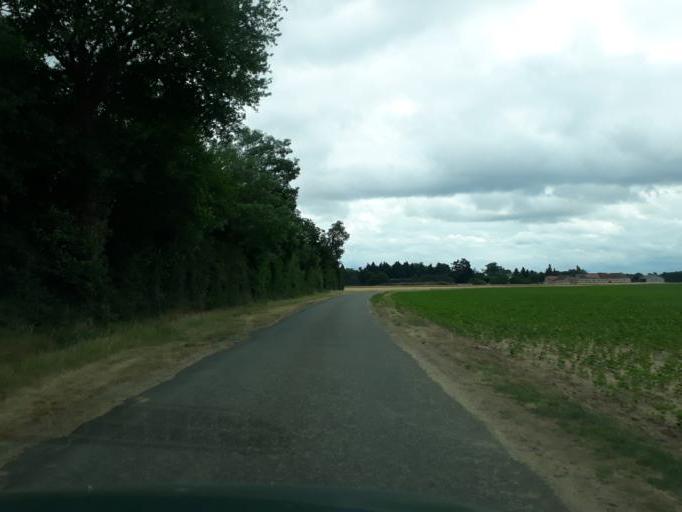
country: FR
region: Centre
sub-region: Departement du Loiret
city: Saint-Cyr-en-Val
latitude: 47.8514
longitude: 1.9821
